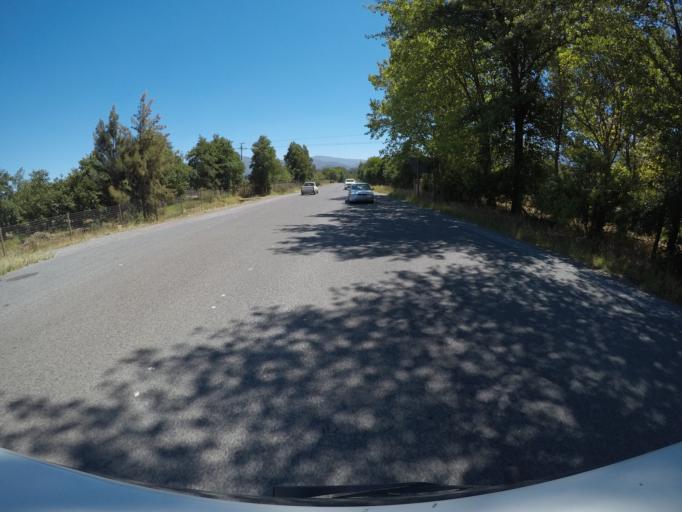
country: ZA
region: Western Cape
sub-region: Overberg District Municipality
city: Grabouw
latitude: -34.1741
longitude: 19.0342
